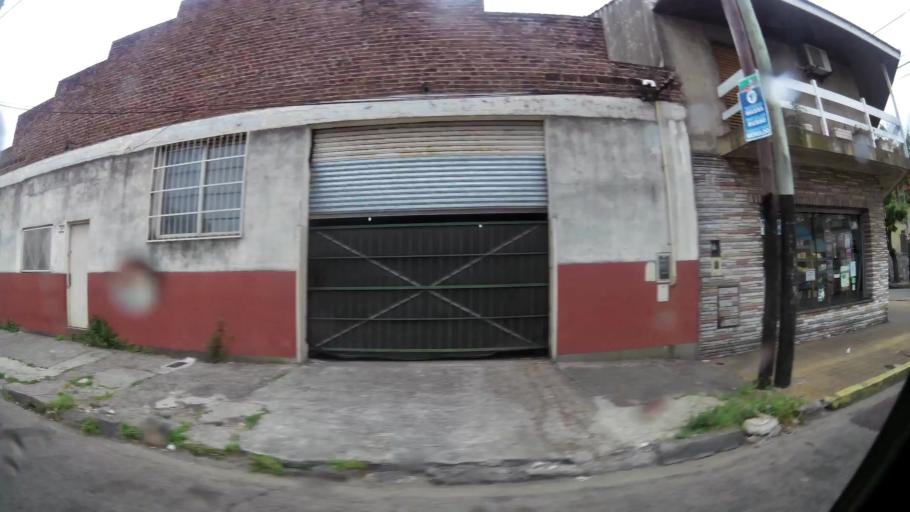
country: AR
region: Buenos Aires
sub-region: Partido de Lanus
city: Lanus
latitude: -34.6856
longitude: -58.4016
